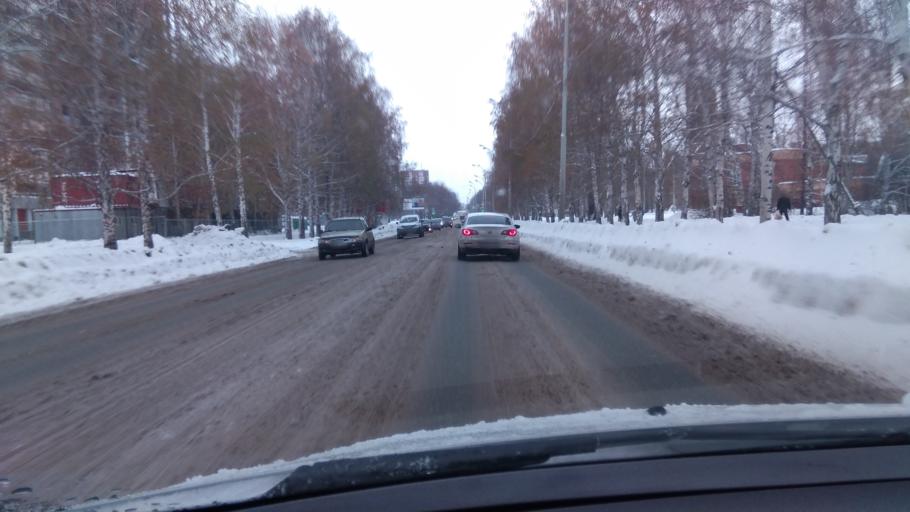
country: RU
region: Sverdlovsk
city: Yekaterinburg
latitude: 56.8134
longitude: 60.5735
